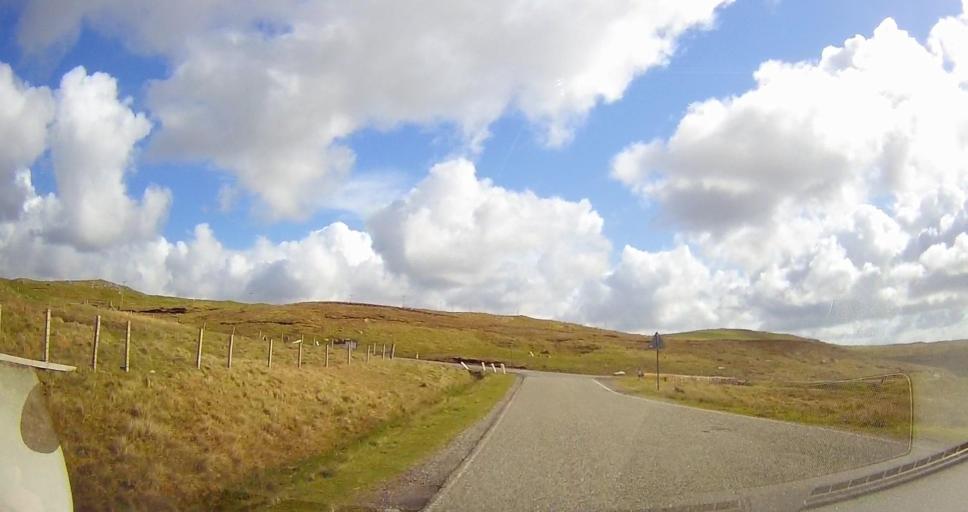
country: GB
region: Scotland
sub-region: Shetland Islands
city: Lerwick
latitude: 60.4904
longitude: -1.3896
